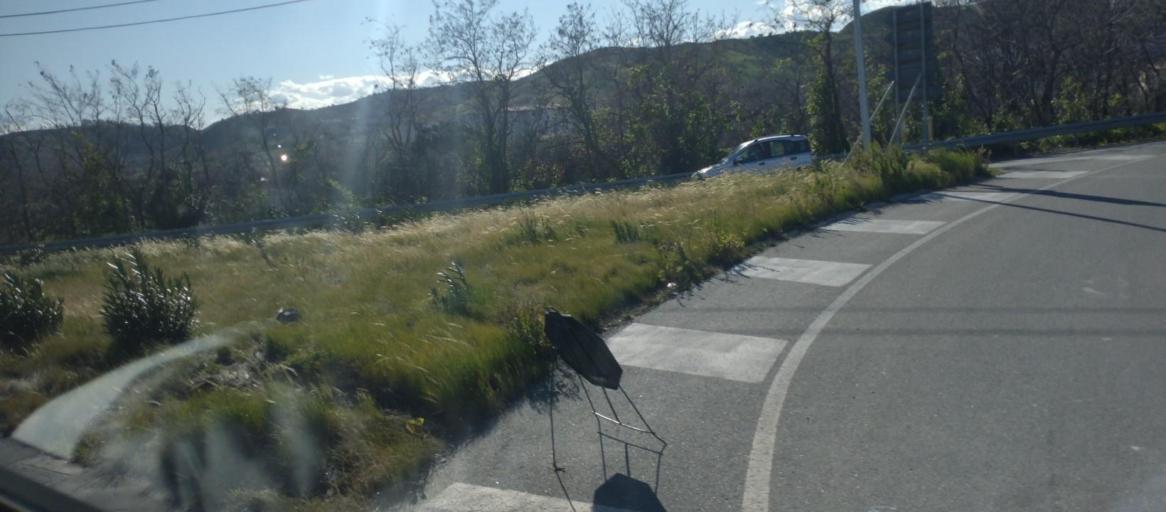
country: IT
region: Calabria
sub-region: Provincia di Catanzaro
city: Catanzaro
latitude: 38.8801
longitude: 16.6046
